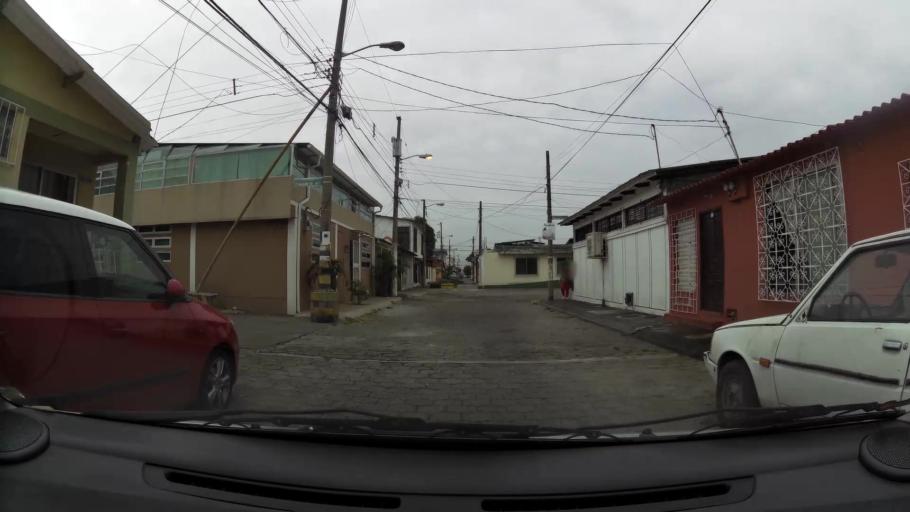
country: EC
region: Guayas
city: Eloy Alfaro
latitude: -2.1353
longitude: -79.8999
